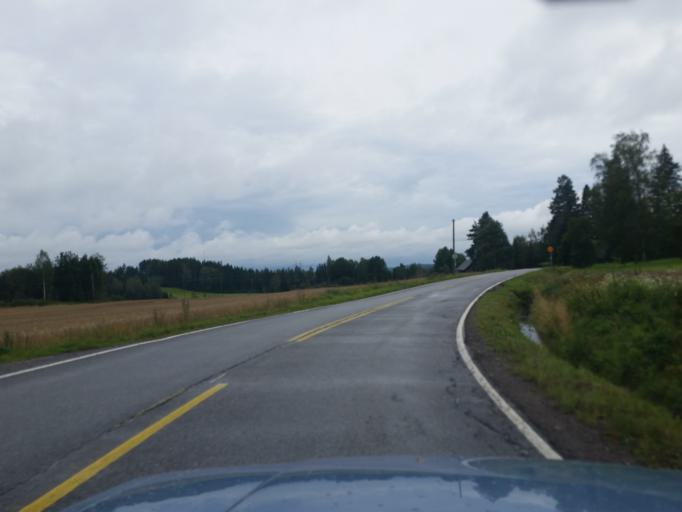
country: FI
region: Uusimaa
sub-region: Helsinki
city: Saukkola
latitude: 60.4962
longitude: 23.9596
